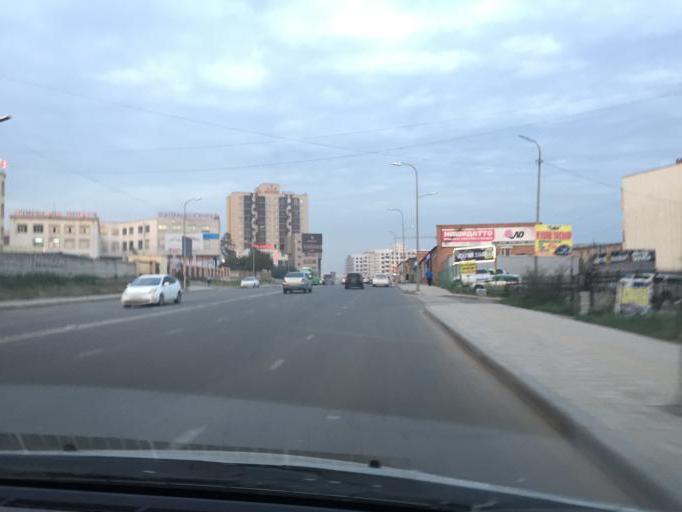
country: MN
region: Ulaanbaatar
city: Ulaanbaatar
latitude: 47.9255
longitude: 106.9452
